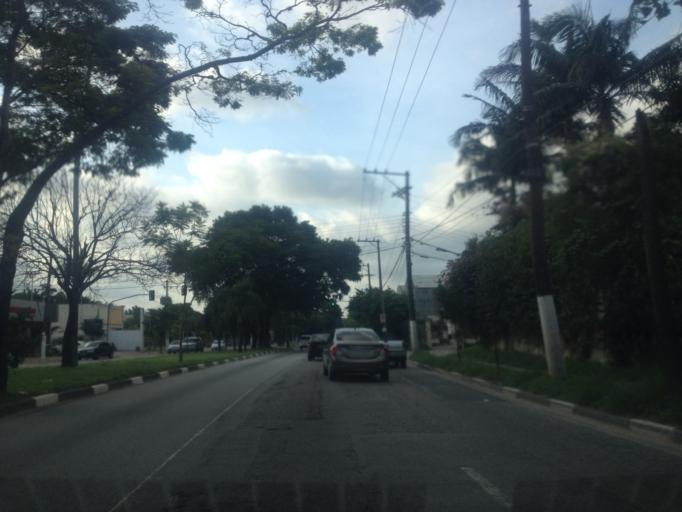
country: BR
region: Sao Paulo
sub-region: Diadema
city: Diadema
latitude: -23.7119
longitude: -46.7105
